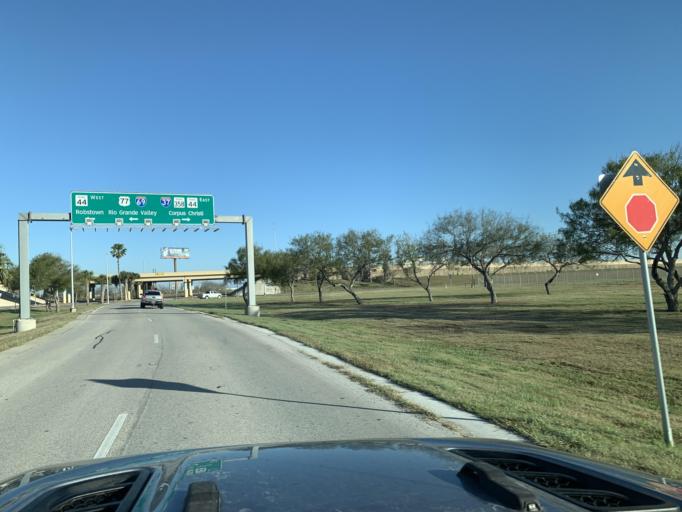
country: US
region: Texas
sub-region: Nueces County
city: Corpus Christi
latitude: 27.7834
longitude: -97.5021
